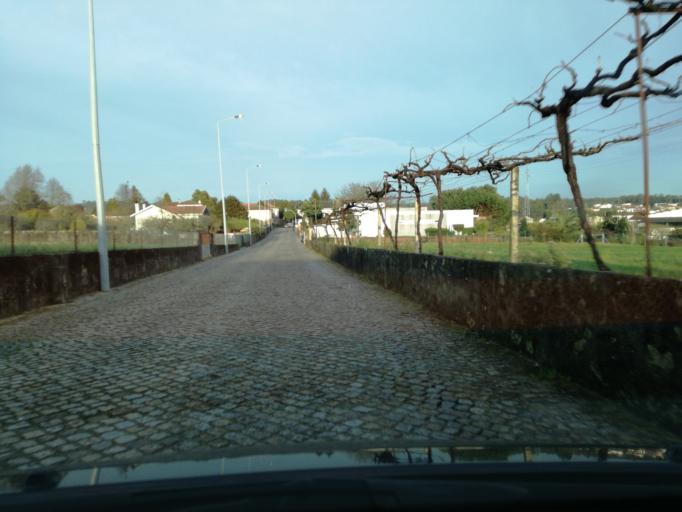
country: PT
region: Porto
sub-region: Maia
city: Anta
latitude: 41.2670
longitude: -8.6088
